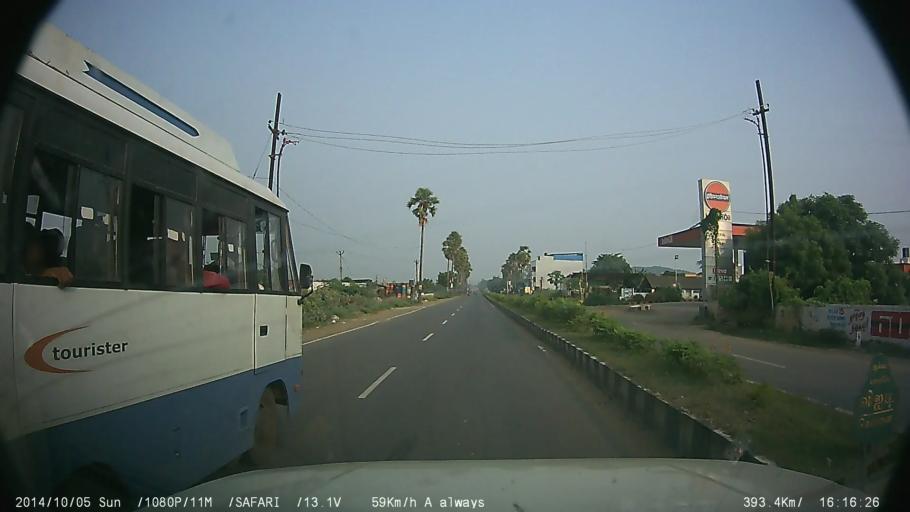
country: IN
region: Tamil Nadu
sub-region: Kancheepuram
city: Vandalur
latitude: 12.8691
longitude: 80.1110
